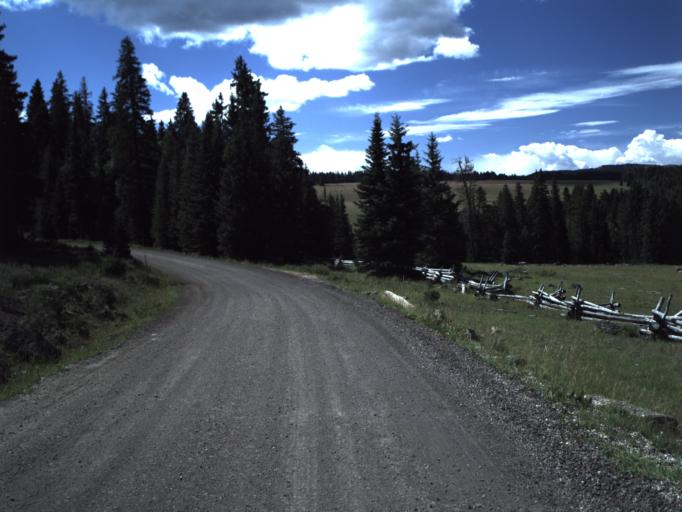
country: US
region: Utah
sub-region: Piute County
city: Junction
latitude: 38.2920
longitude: -112.3596
